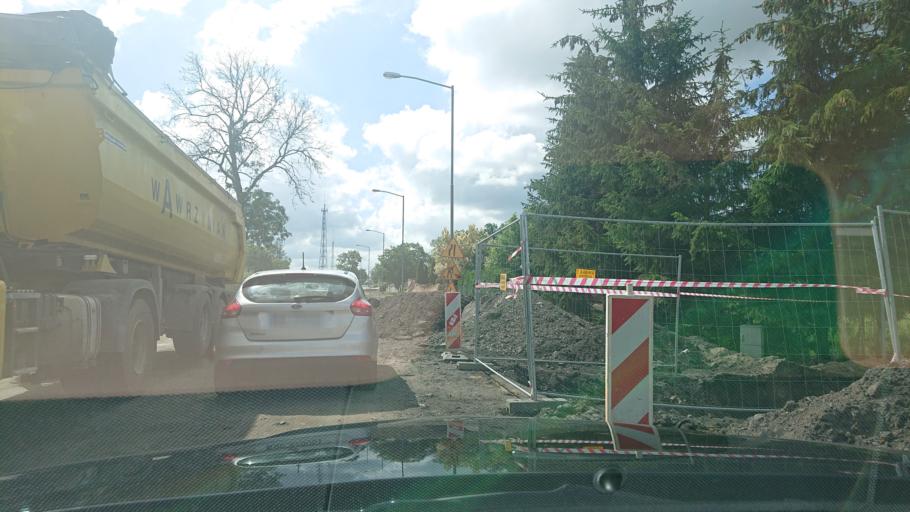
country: PL
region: Greater Poland Voivodeship
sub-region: Powiat gnieznienski
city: Gniezno
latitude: 52.5431
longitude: 17.6310
